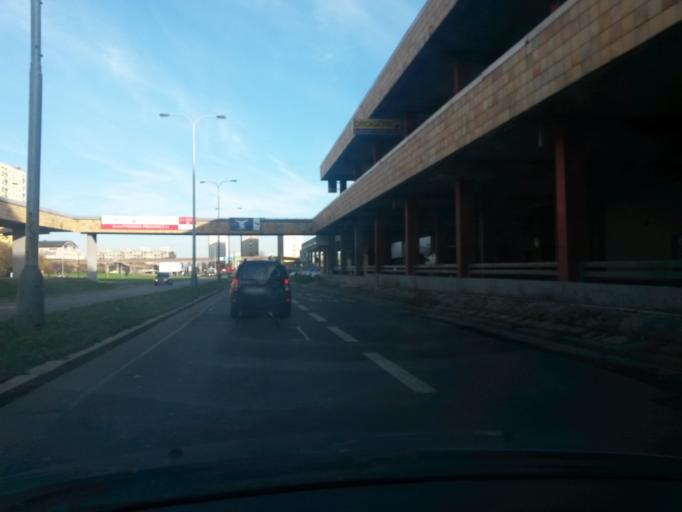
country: CZ
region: Central Bohemia
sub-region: Okres Praha-Zapad
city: Pruhonice
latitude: 50.0254
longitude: 14.5173
